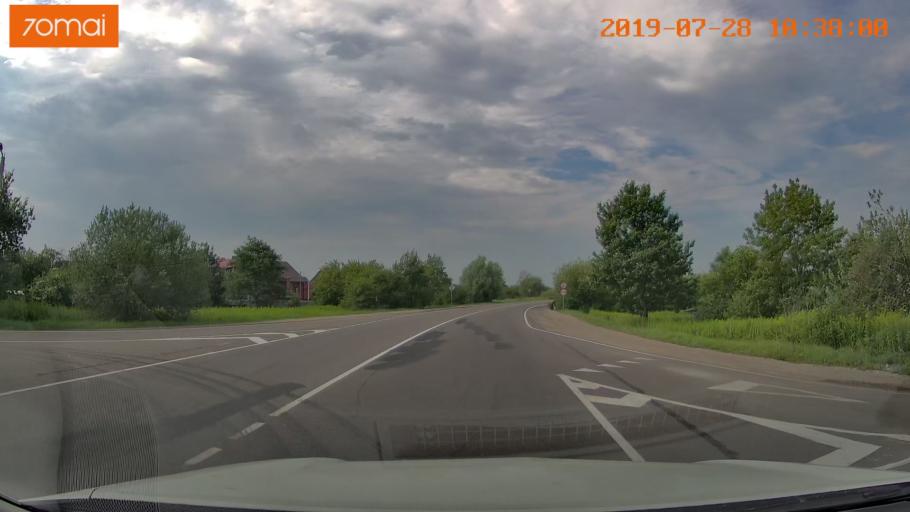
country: RU
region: Kaliningrad
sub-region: Gorod Kaliningrad
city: Kaliningrad
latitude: 54.7270
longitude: 20.4043
